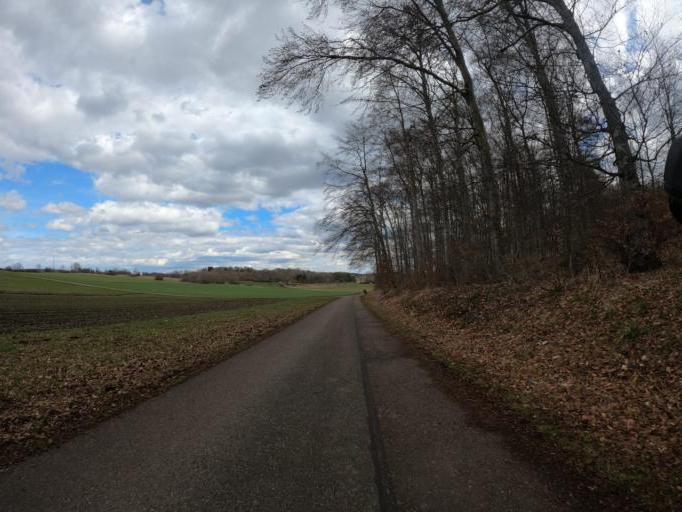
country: DE
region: Baden-Wuerttemberg
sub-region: Tuebingen Region
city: Burladingen
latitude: 48.3786
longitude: 9.1684
